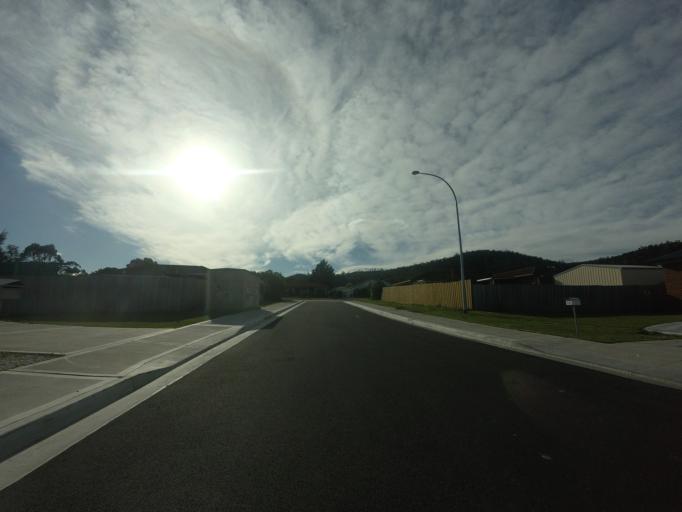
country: AU
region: Tasmania
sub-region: Clarence
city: Rokeby
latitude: -42.9020
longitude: 147.4536
